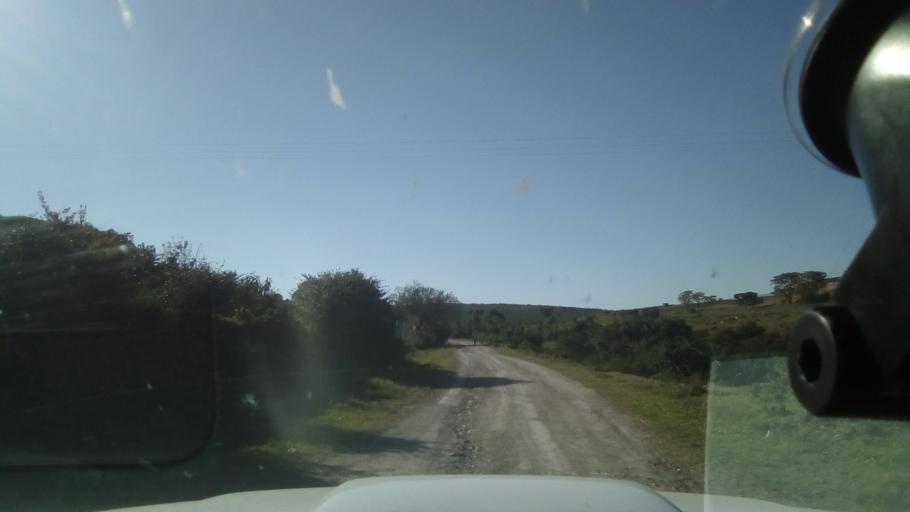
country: ZA
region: Eastern Cape
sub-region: Buffalo City Metropolitan Municipality
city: Bhisho
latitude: -32.7992
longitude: 27.3416
